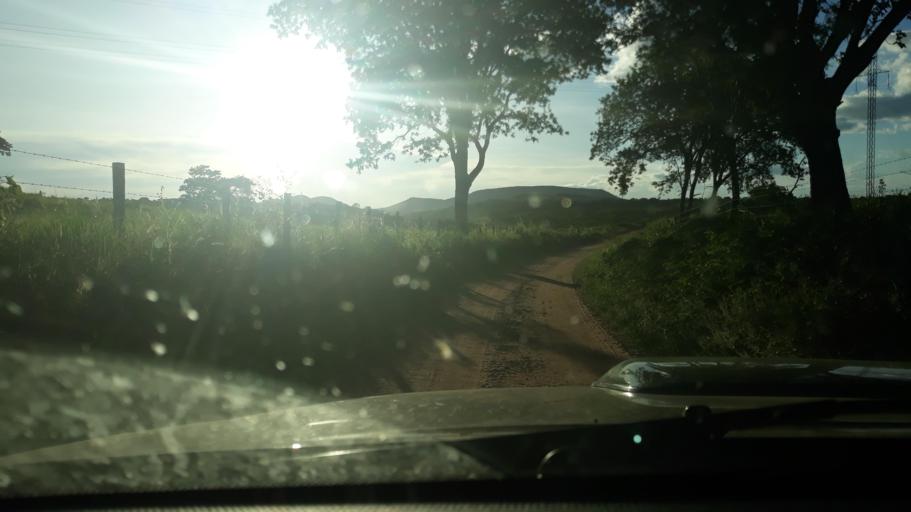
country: BR
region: Bahia
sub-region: Riacho De Santana
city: Riacho de Santana
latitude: -13.8466
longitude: -42.7519
